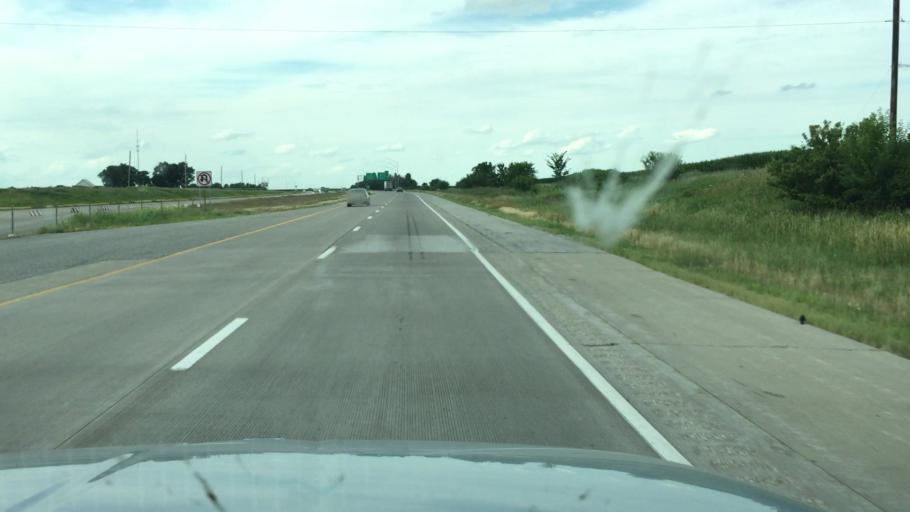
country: US
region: Iowa
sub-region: Scott County
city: Walcott
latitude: 41.5817
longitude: -90.6763
